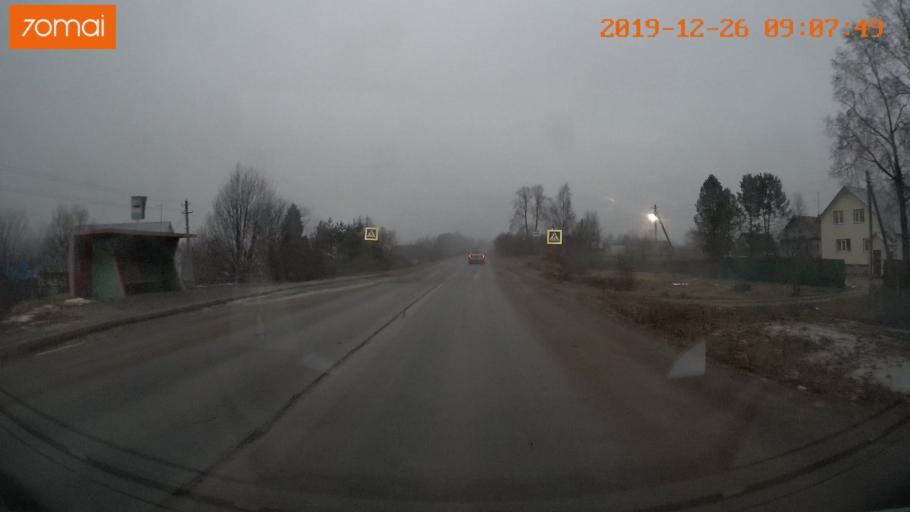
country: RU
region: Vologda
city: Gryazovets
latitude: 58.8501
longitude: 40.2468
